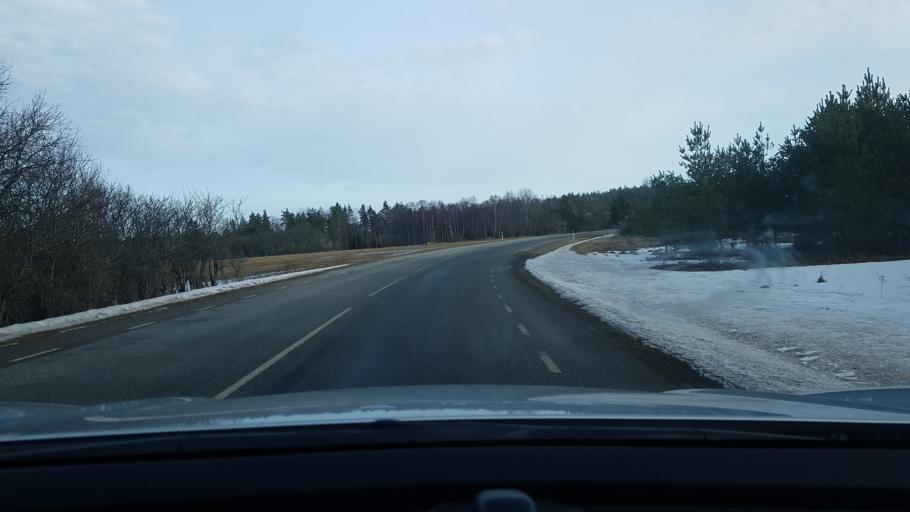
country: EE
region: Saare
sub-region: Kuressaare linn
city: Kuressaare
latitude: 58.4033
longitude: 22.6434
